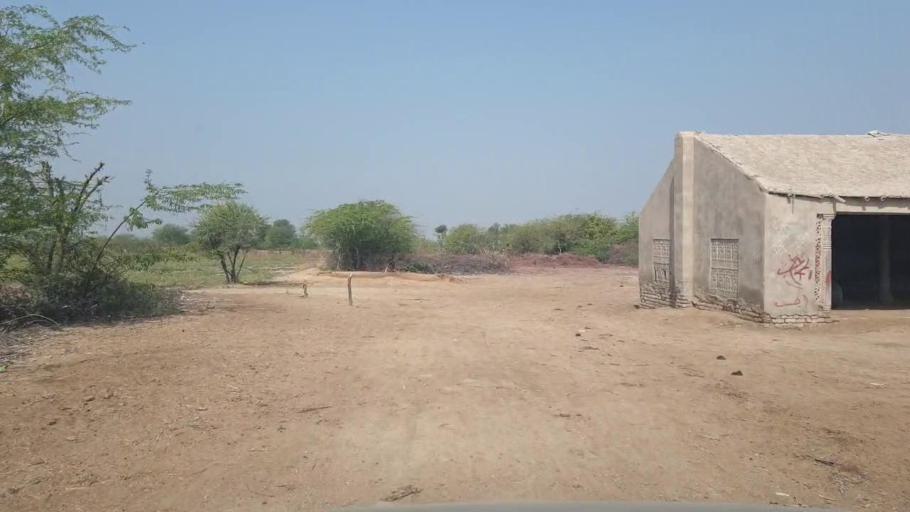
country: PK
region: Sindh
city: Dhoro Naro
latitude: 25.4476
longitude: 69.6651
